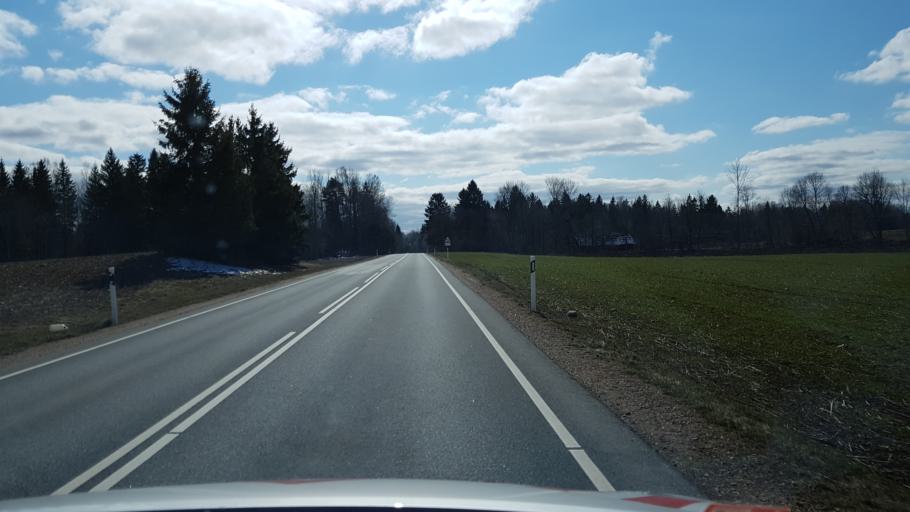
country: EE
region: Laeaene-Virumaa
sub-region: Tapa vald
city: Tapa
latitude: 59.3613
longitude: 26.0004
